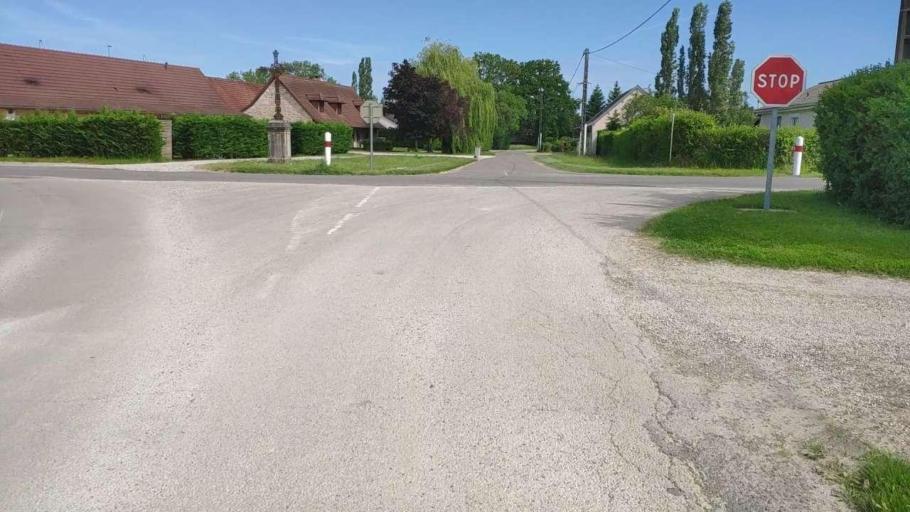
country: FR
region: Franche-Comte
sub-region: Departement du Jura
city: Bletterans
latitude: 46.7095
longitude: 5.4455
